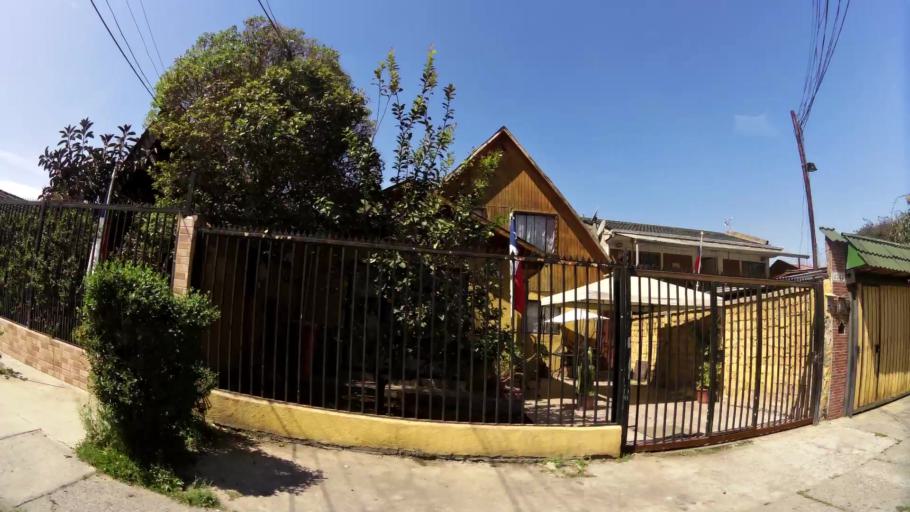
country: CL
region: Santiago Metropolitan
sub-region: Provincia de Santiago
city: La Pintana
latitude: -33.5333
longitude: -70.6559
